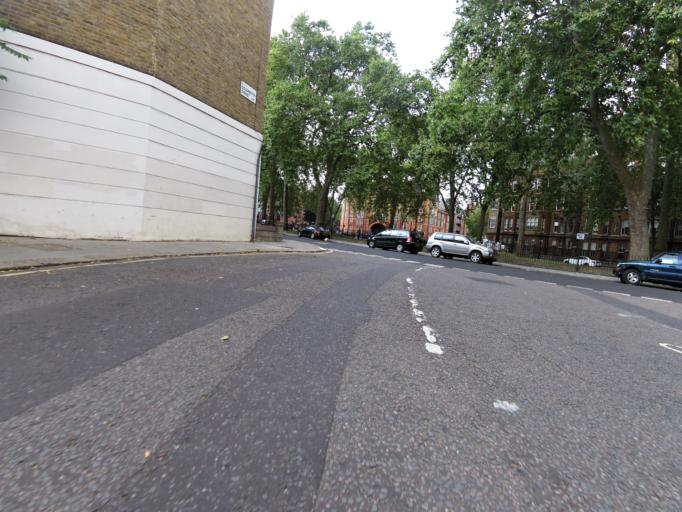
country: GB
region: England
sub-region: Greater London
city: Camden Town
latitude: 51.5348
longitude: -0.1320
